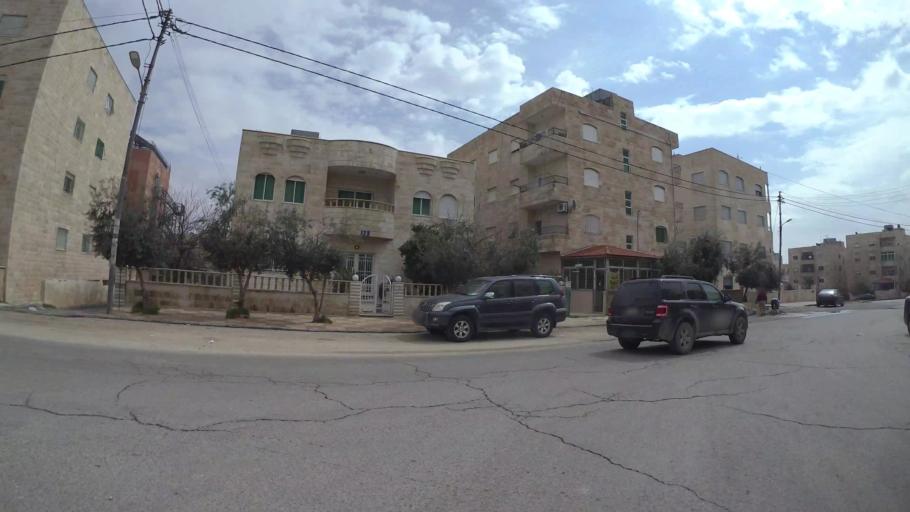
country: JO
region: Amman
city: Amman
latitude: 31.9882
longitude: 35.9282
